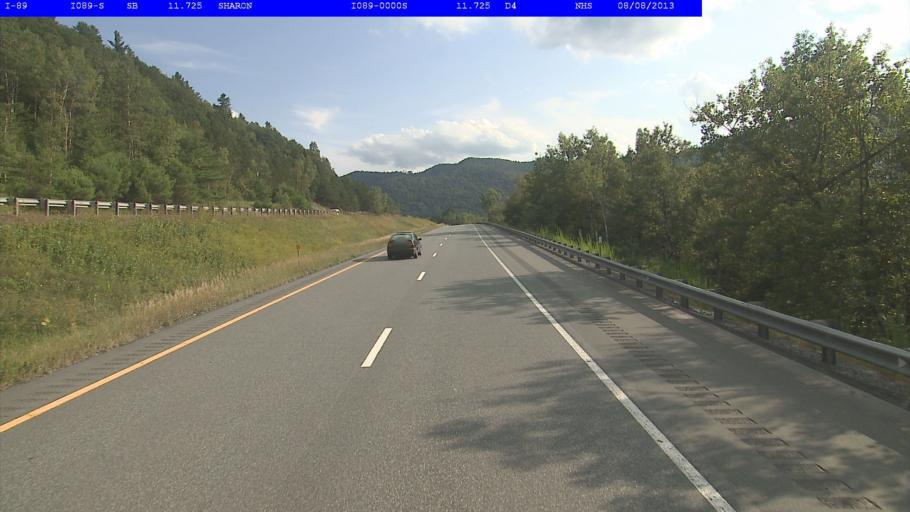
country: US
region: Vermont
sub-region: Windsor County
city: Woodstock
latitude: 43.7642
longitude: -72.4464
